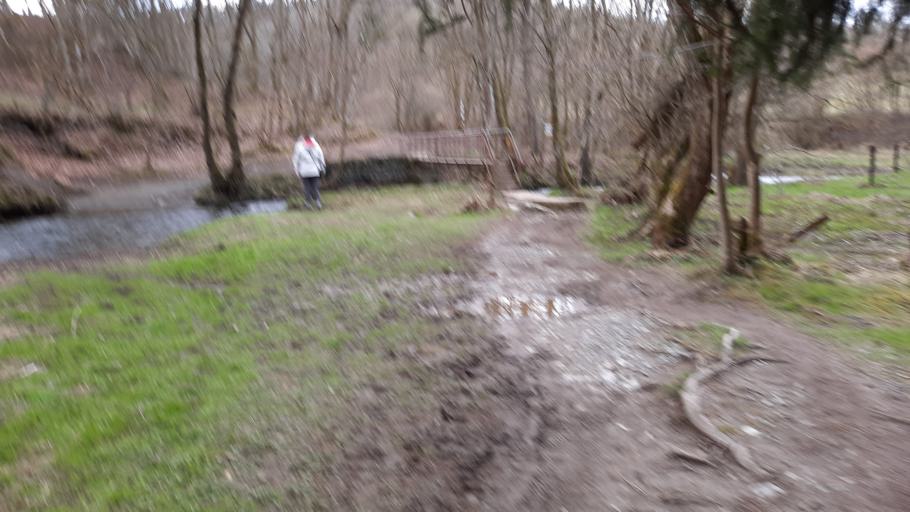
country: BE
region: Wallonia
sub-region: Province du Luxembourg
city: Houffalize
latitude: 50.1309
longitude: 5.8033
